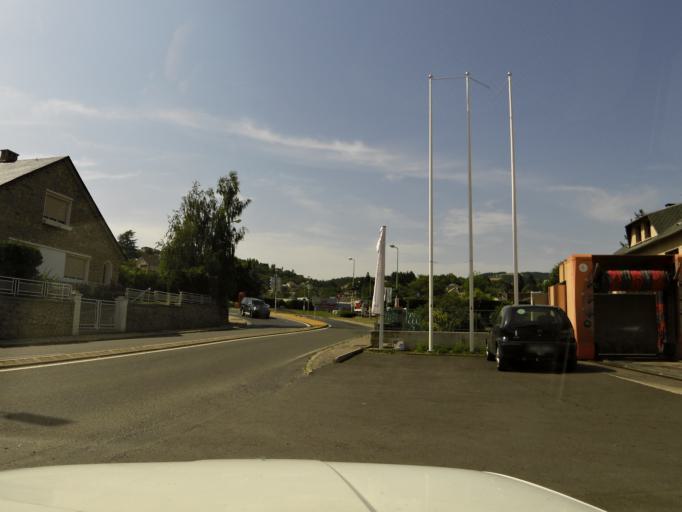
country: FR
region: Languedoc-Roussillon
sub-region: Departement de la Lozere
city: Marvejols
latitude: 44.5632
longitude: 3.2919
